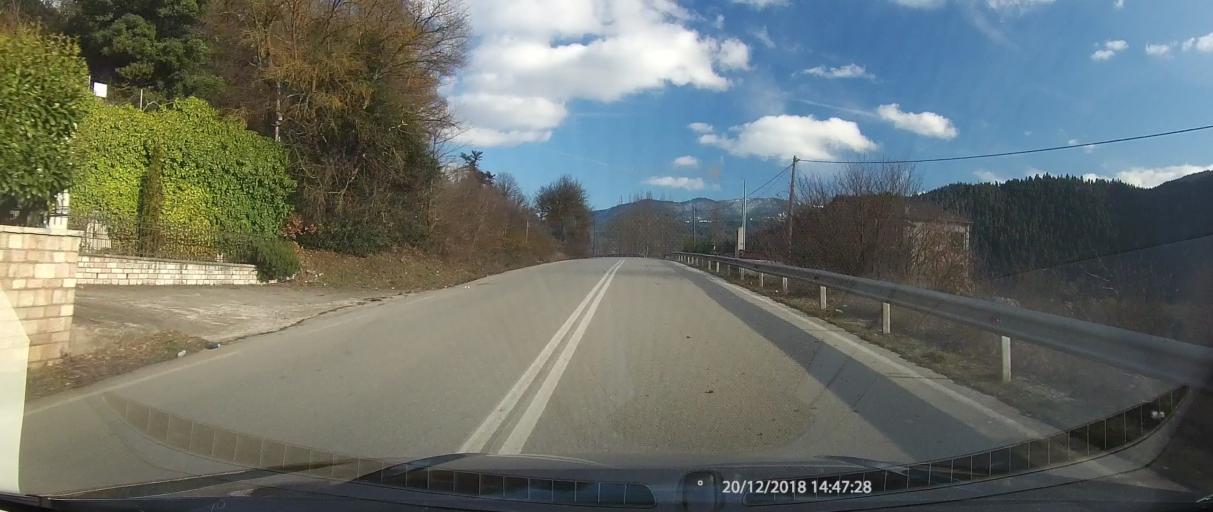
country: GR
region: Central Greece
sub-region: Nomos Evrytanias
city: Karpenisi
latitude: 38.9016
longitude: 21.7790
